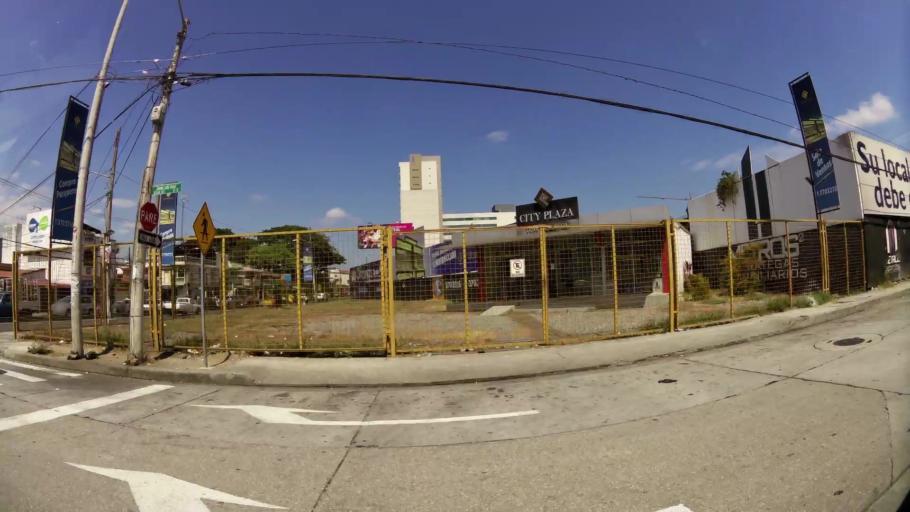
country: EC
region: Guayas
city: Guayaquil
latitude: -2.1421
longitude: -79.9096
